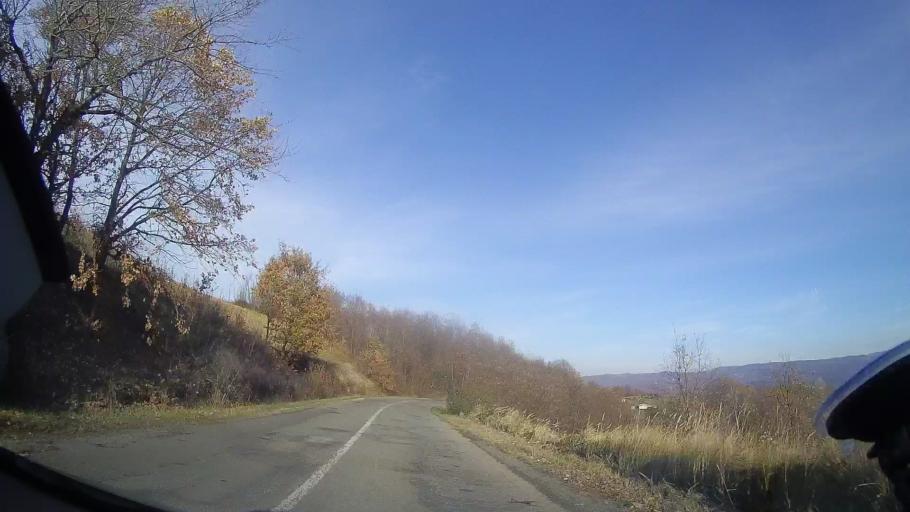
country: RO
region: Bihor
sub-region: Comuna Brusturi
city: Brusturi
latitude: 47.1060
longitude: 22.2531
